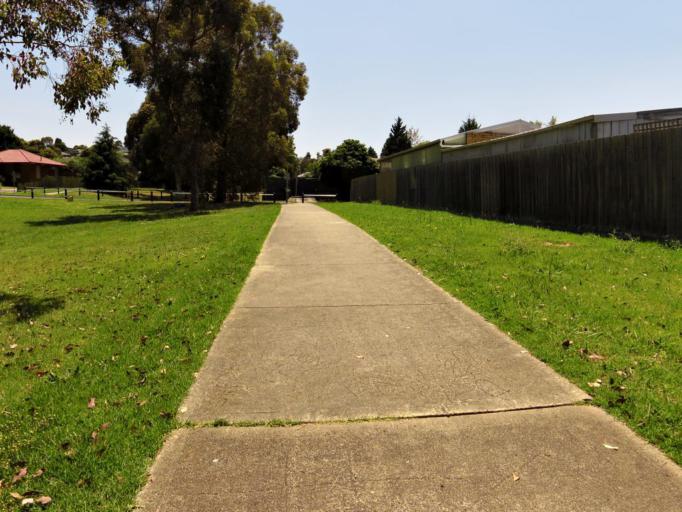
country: AU
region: Victoria
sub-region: Casey
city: Endeavour Hills
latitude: -37.9900
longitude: 145.2591
